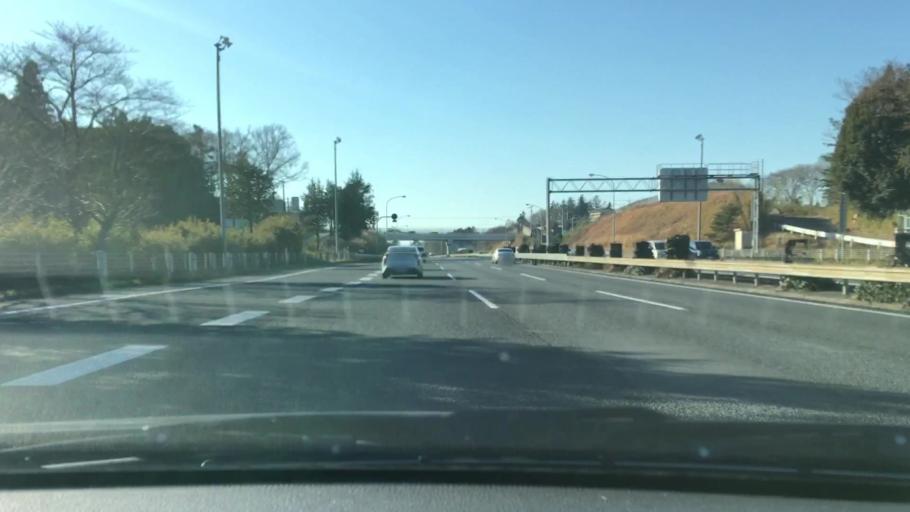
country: JP
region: Chiba
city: Sakura
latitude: 35.6868
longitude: 140.2343
